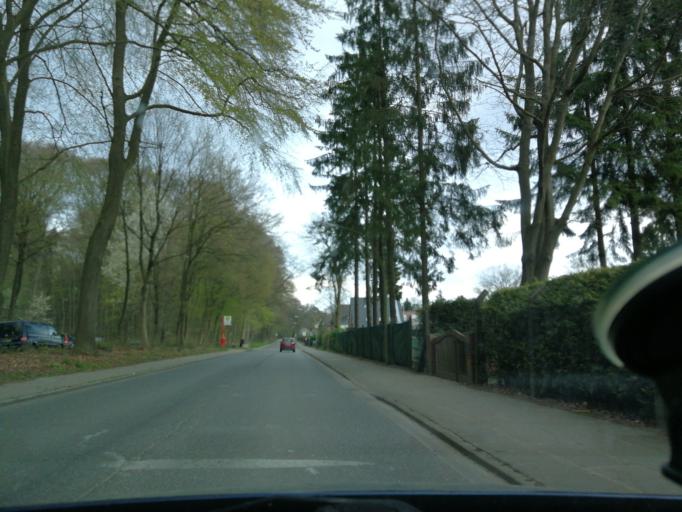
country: DE
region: Hamburg
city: Harburg
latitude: 53.4575
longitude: 9.9354
